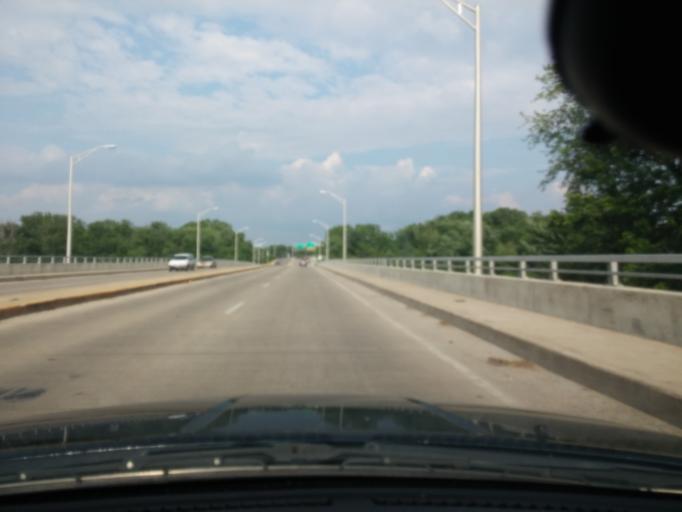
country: US
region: Indiana
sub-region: Tippecanoe County
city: West Lafayette
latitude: 40.4252
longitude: -86.8982
